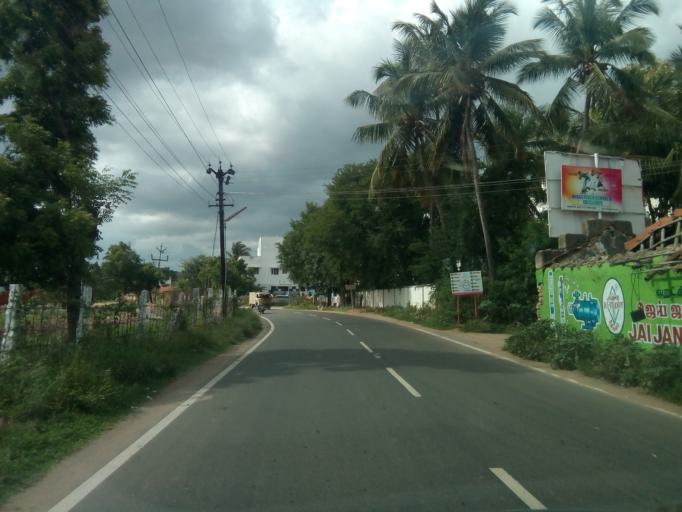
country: IN
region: Tamil Nadu
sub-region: Coimbatore
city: Irugur
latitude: 11.0833
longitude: 77.0351
